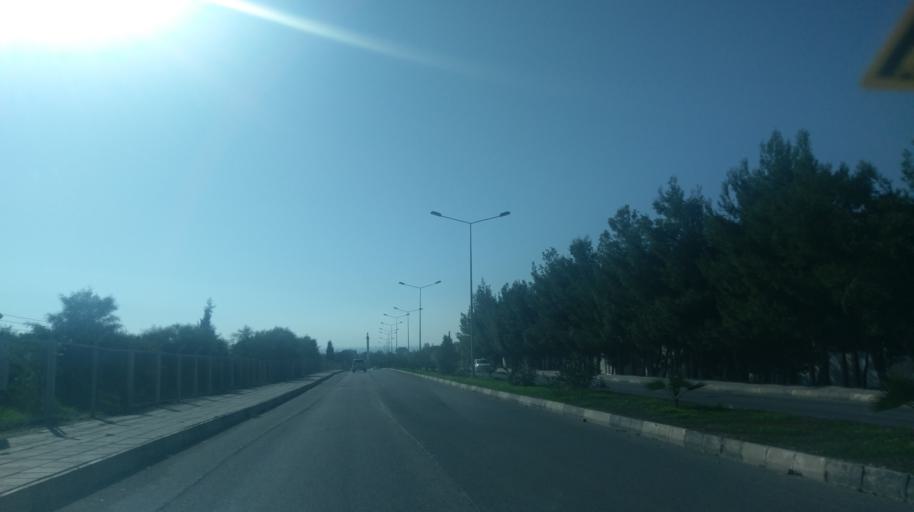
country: CY
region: Lefkosia
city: Nicosia
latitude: 35.2253
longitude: 33.3279
